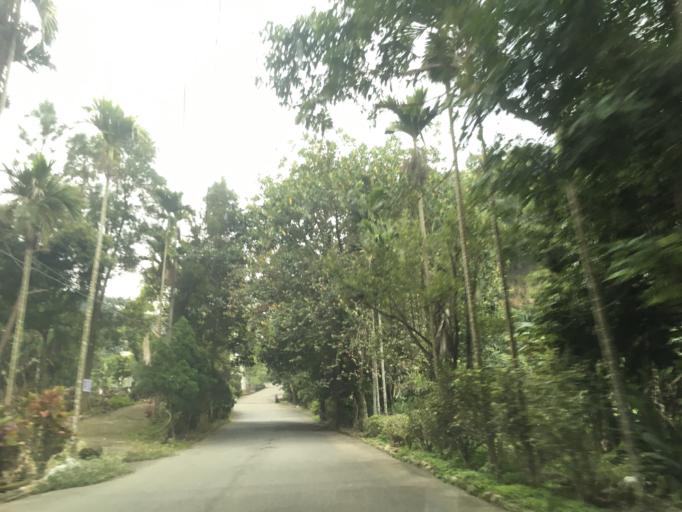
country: TW
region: Taiwan
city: Daxi
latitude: 24.8875
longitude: 121.3008
